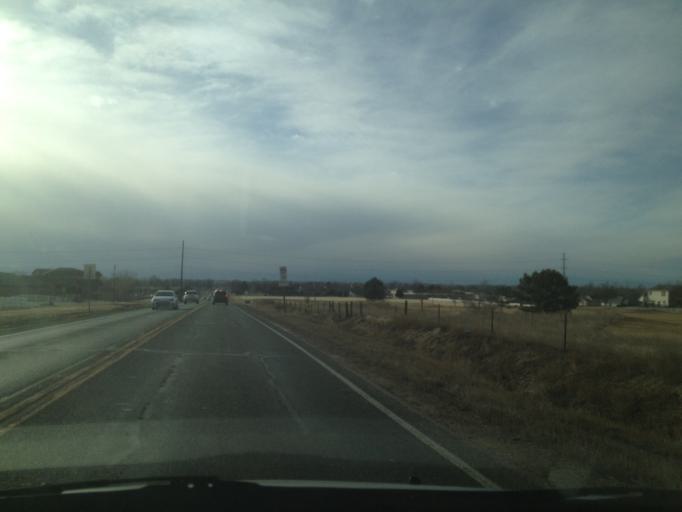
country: US
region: Colorado
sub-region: Weld County
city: Fort Lupton
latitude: 40.0802
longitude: -104.7974
